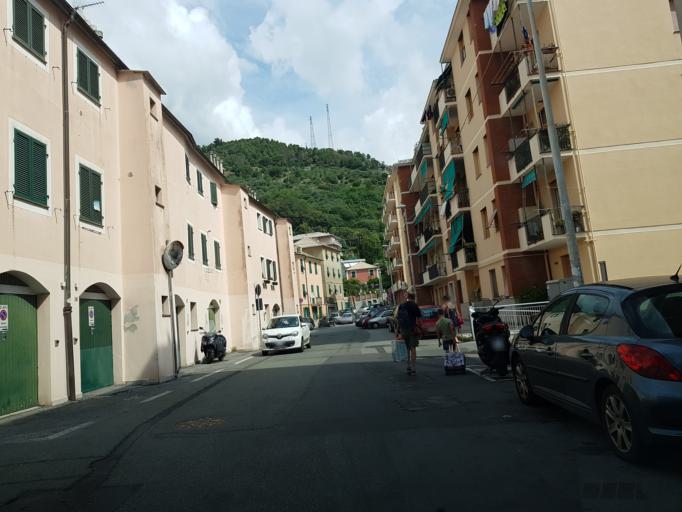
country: IT
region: Liguria
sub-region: Provincia di Genova
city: San Teodoro
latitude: 44.4329
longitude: 8.8516
